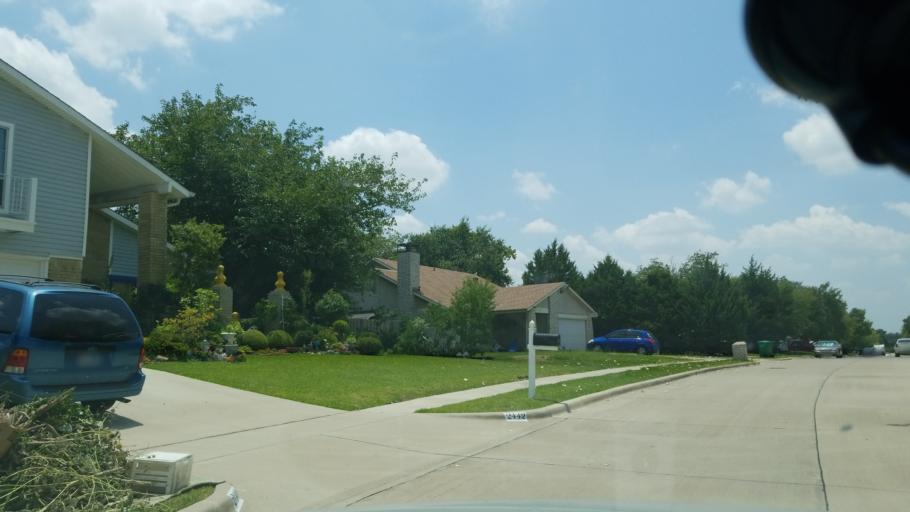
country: US
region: Texas
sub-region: Dallas County
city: Carrollton
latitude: 32.9690
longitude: -96.8728
